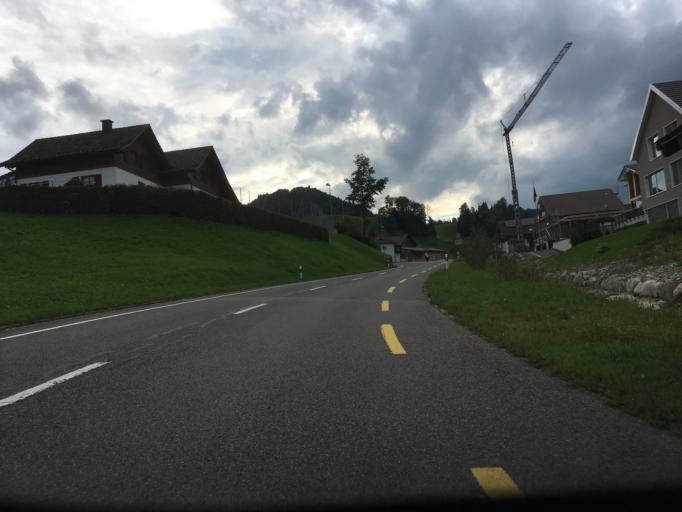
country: CH
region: Thurgau
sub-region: Muenchwilen District
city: Fischingen
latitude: 47.3717
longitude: 8.9881
